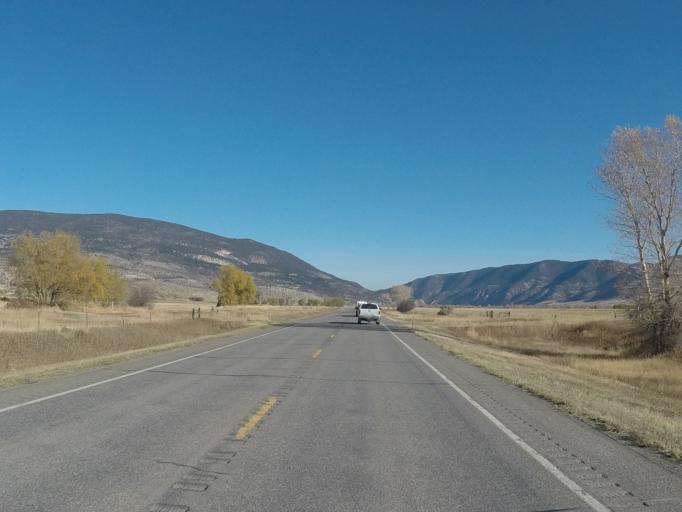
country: US
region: Montana
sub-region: Park County
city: Livingston
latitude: 45.5396
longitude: -110.6017
